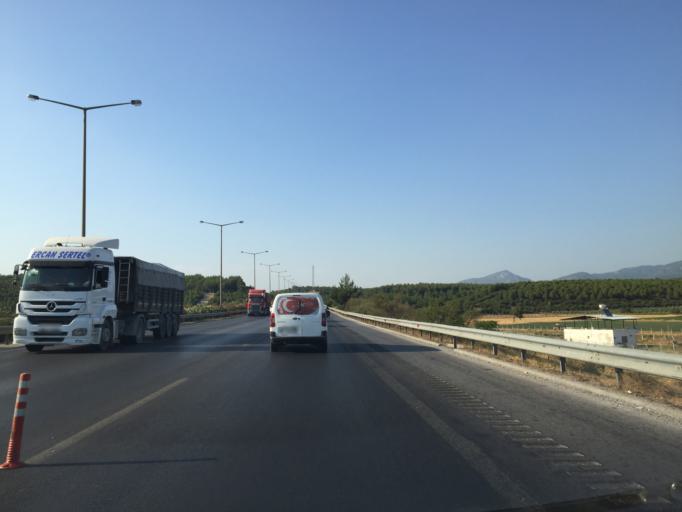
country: TR
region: Izmir
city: Menderes
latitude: 38.2803
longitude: 27.2248
